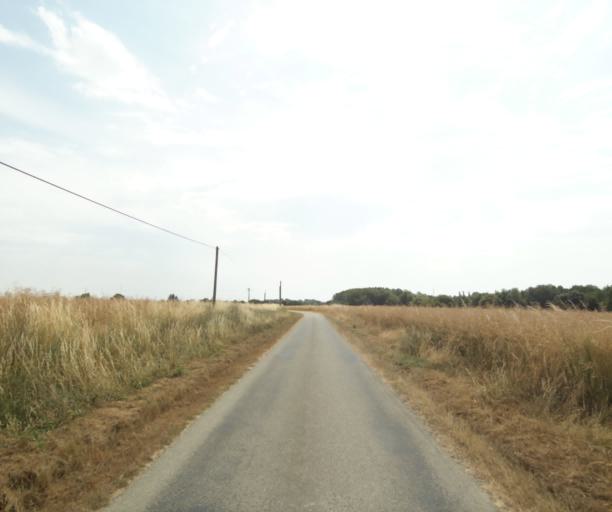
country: FR
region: Centre
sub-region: Departement d'Eure-et-Loir
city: La Bazoche-Gouet
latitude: 48.1844
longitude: 0.9522
